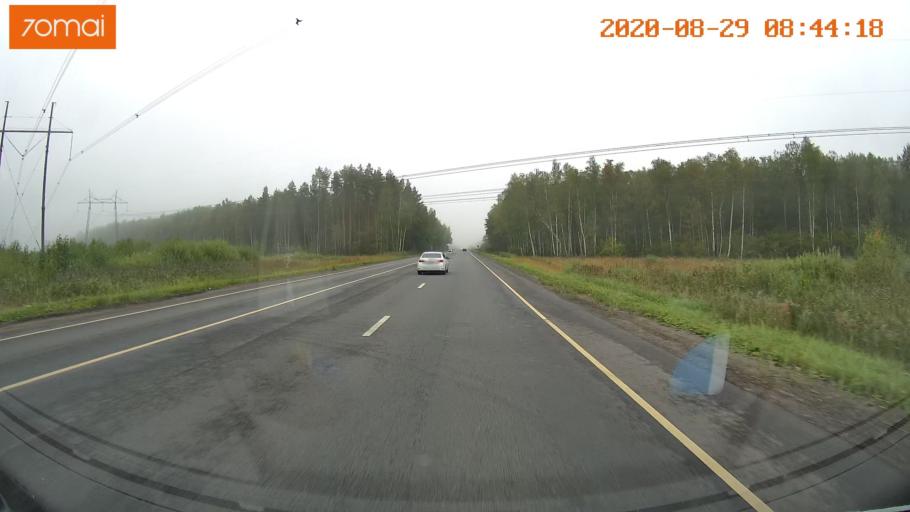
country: RU
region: Ivanovo
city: Rodniki
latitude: 57.1164
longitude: 41.7874
